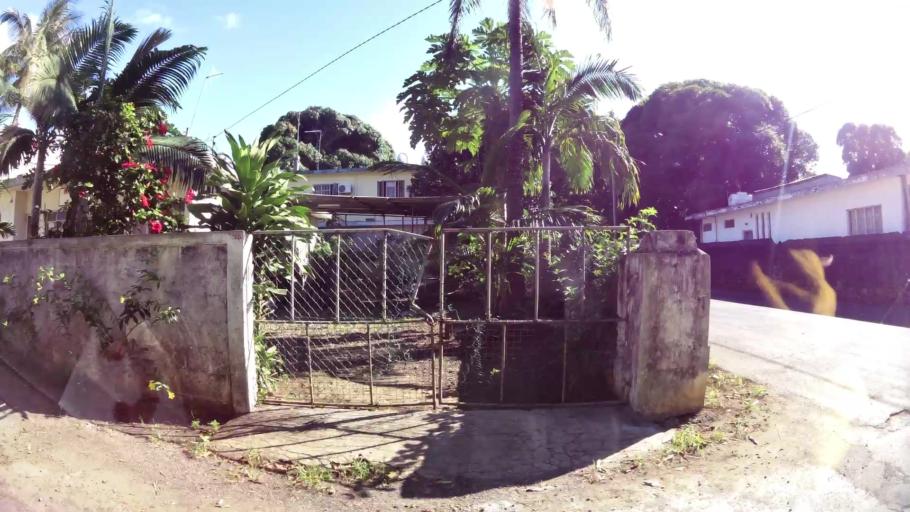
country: MU
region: Grand Port
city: Mahebourg
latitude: -20.4109
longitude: 57.7081
